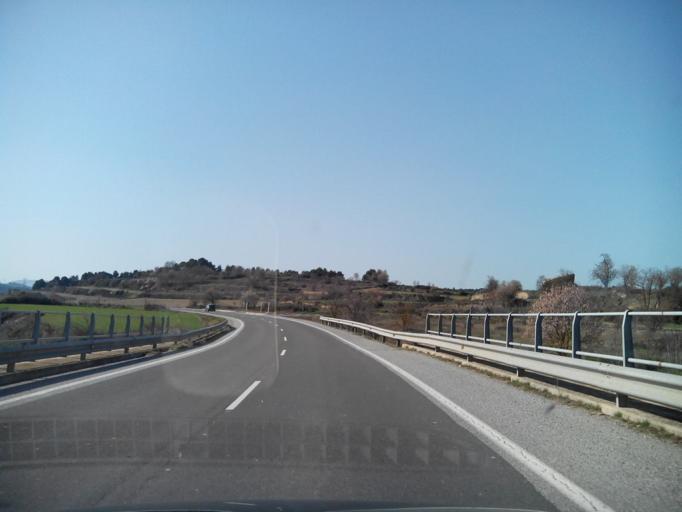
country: ES
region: Catalonia
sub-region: Provincia de Tarragona
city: Fores
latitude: 41.4746
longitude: 1.2771
